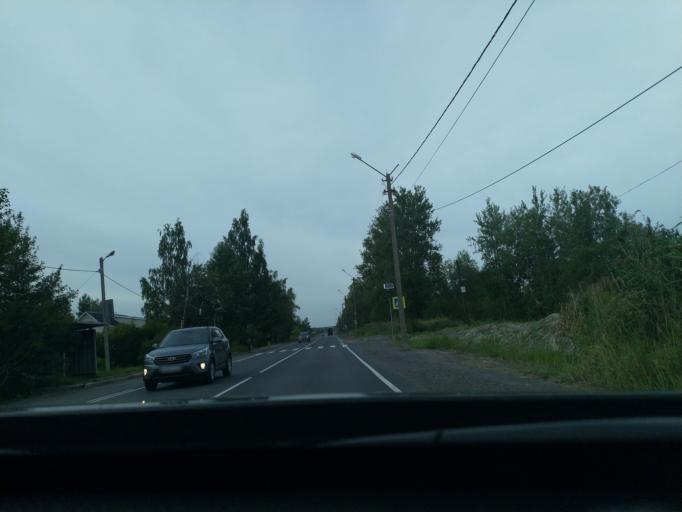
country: RU
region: Leningrad
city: Nikol'skoye
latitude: 59.7159
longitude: 30.7792
